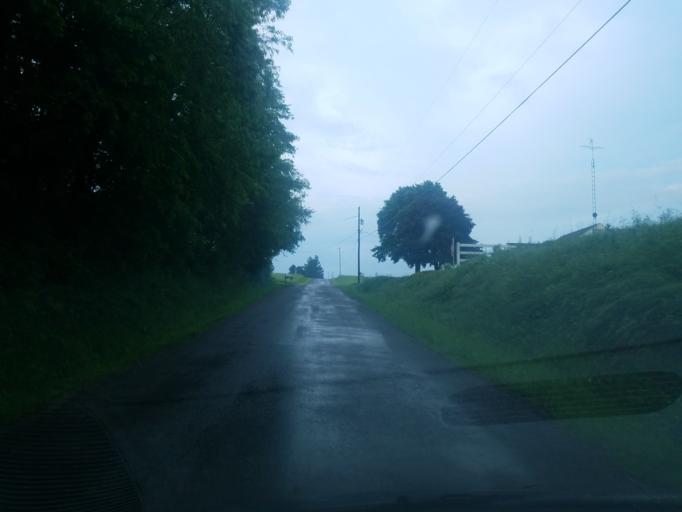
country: US
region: Ohio
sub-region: Mahoning County
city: Sebring
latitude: 40.7929
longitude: -80.9555
